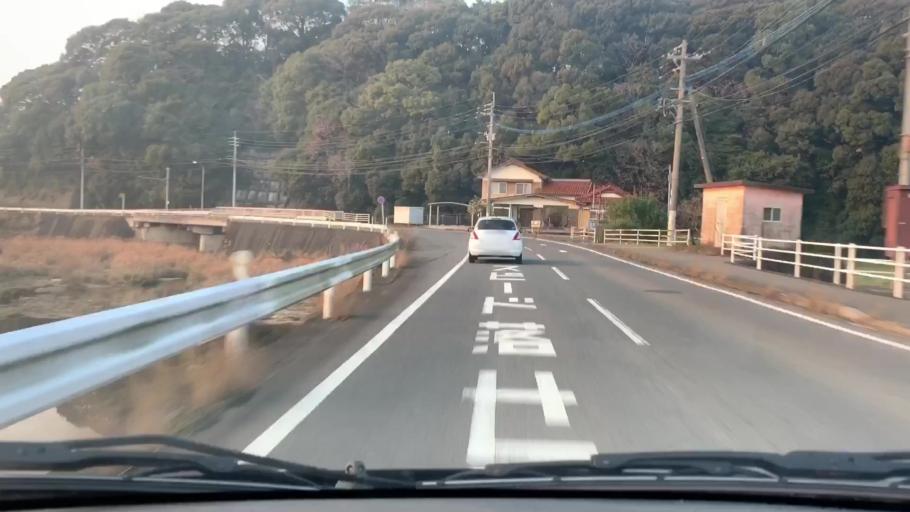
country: JP
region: Saga Prefecture
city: Imaricho-ko
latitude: 33.2714
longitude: 129.8948
